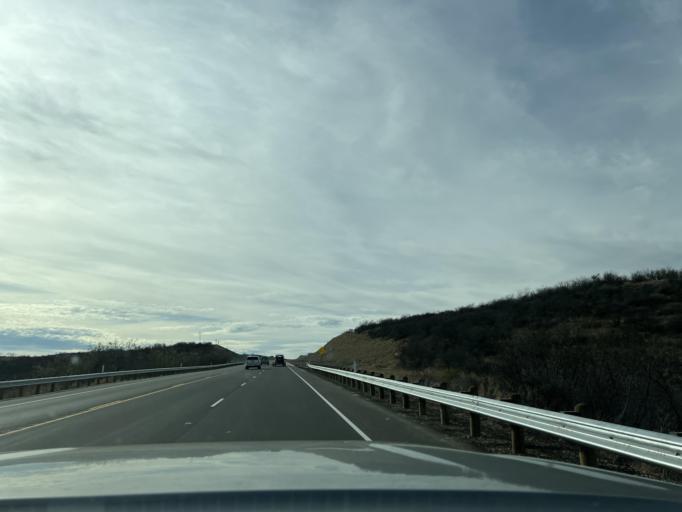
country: US
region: Texas
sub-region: Shackelford County
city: Albany
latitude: 32.7090
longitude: -99.3717
